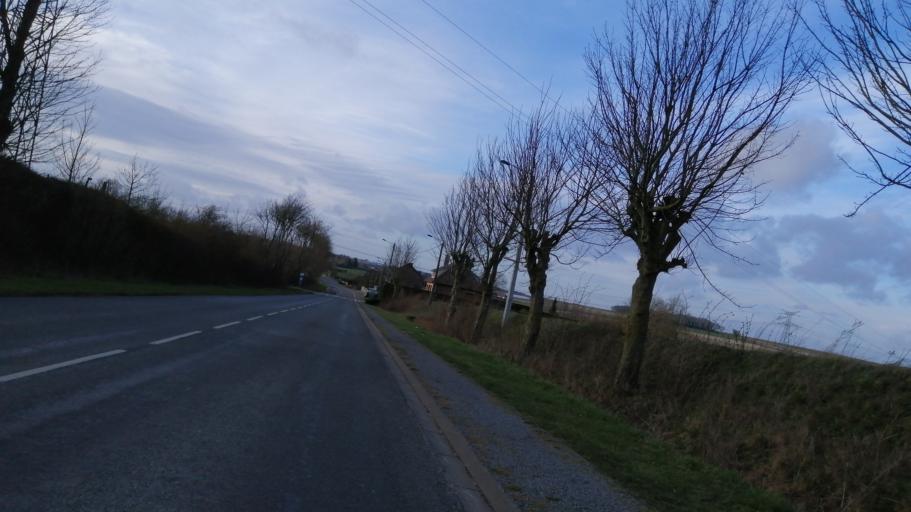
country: FR
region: Nord-Pas-de-Calais
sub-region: Departement du Pas-de-Calais
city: Beaurains
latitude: 50.2481
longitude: 2.8130
